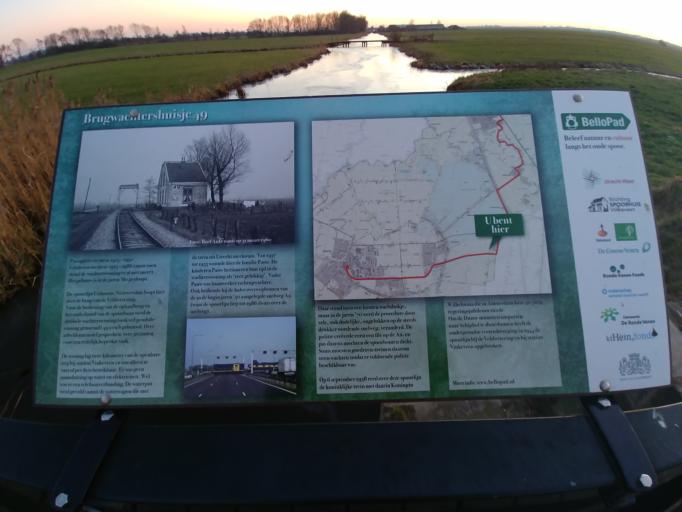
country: NL
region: Utrecht
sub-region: Stichtse Vecht
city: Breukelen
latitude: 52.2113
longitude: 4.9651
